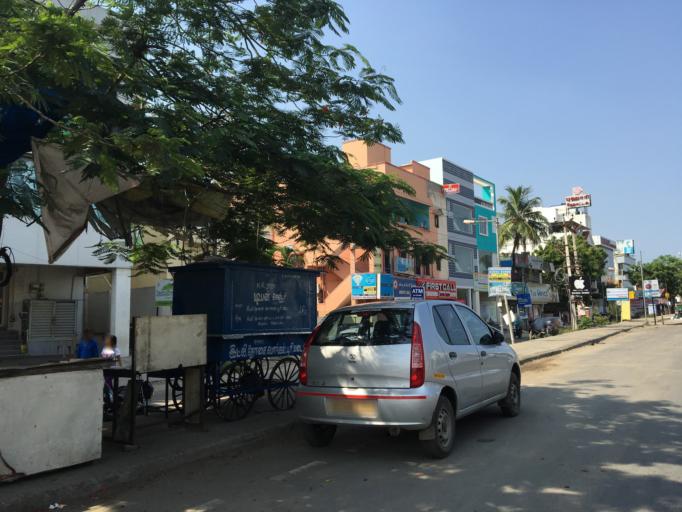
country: IN
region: Tamil Nadu
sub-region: Kancheepuram
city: Perungudi
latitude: 12.9788
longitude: 80.2258
